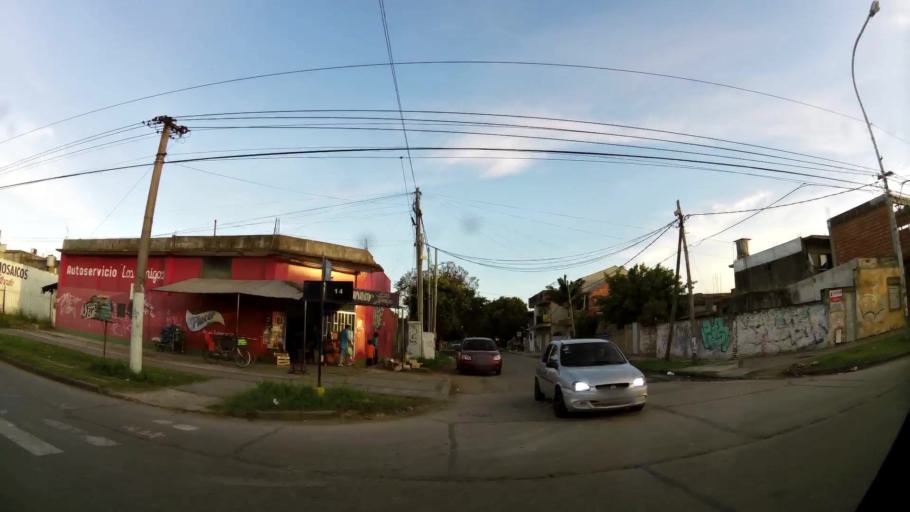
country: AR
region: Buenos Aires
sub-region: Partido de Quilmes
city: Quilmes
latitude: -34.7740
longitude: -58.2325
